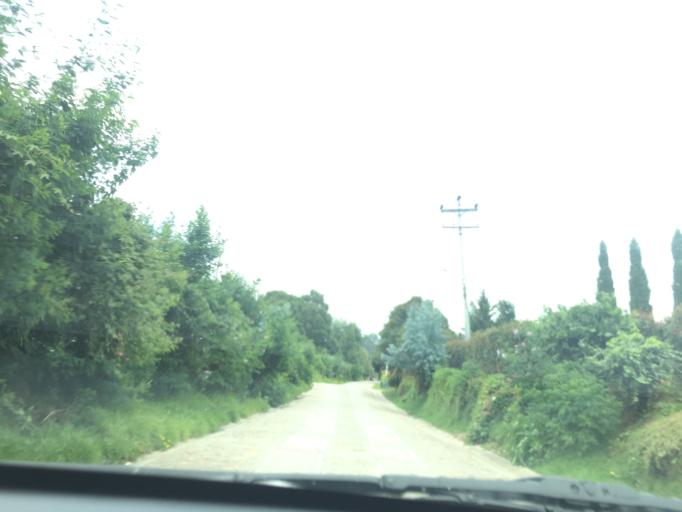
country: CO
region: Cundinamarca
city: El Rosal
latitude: 4.8809
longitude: -74.2585
